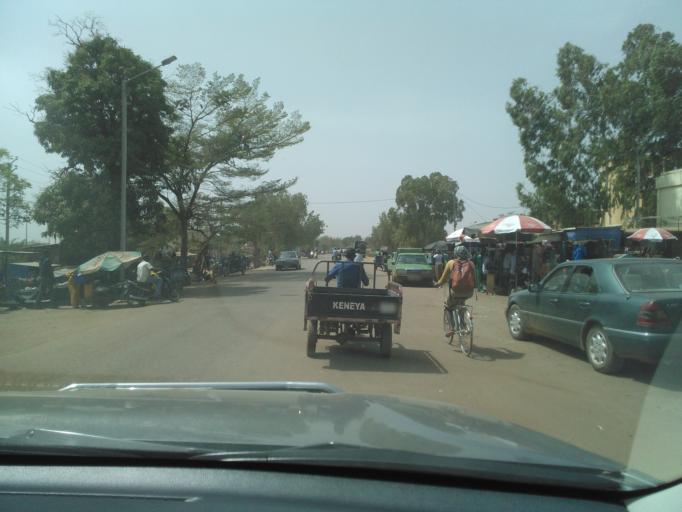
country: BF
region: Centre
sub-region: Kadiogo Province
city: Ouagadougou
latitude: 12.3556
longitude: -1.5354
